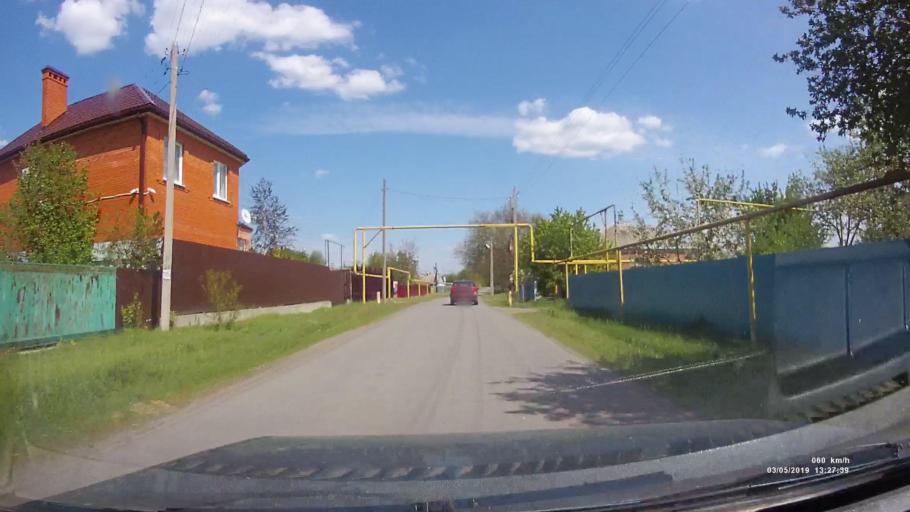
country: RU
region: Rostov
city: Semikarakorsk
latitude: 47.5754
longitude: 40.8359
